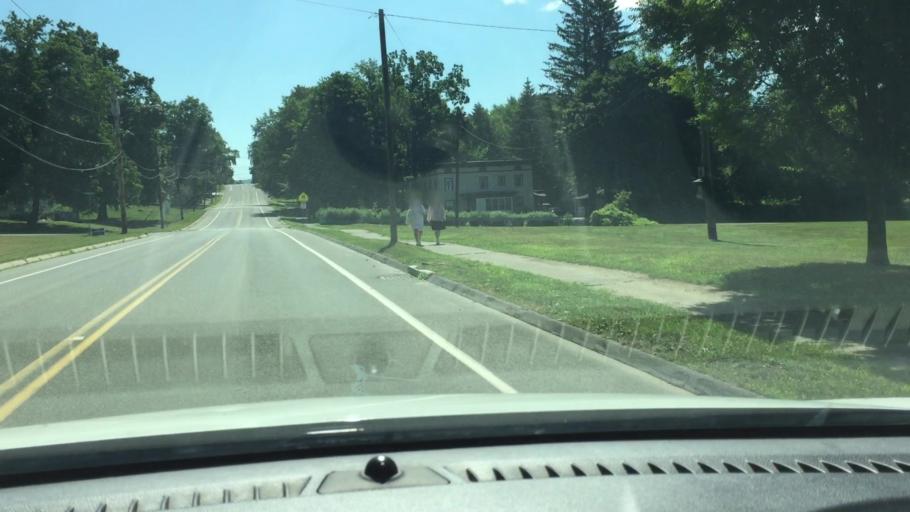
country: US
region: Massachusetts
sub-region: Berkshire County
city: Pittsfield
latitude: 42.4366
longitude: -73.2412
